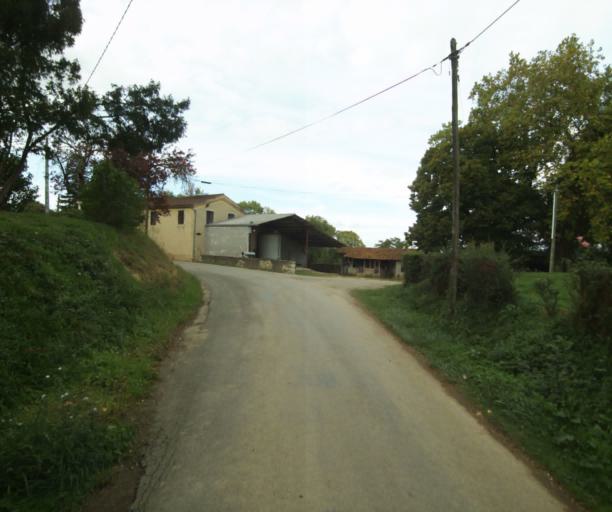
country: FR
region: Midi-Pyrenees
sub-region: Departement du Gers
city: Gondrin
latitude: 43.8719
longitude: 0.2495
